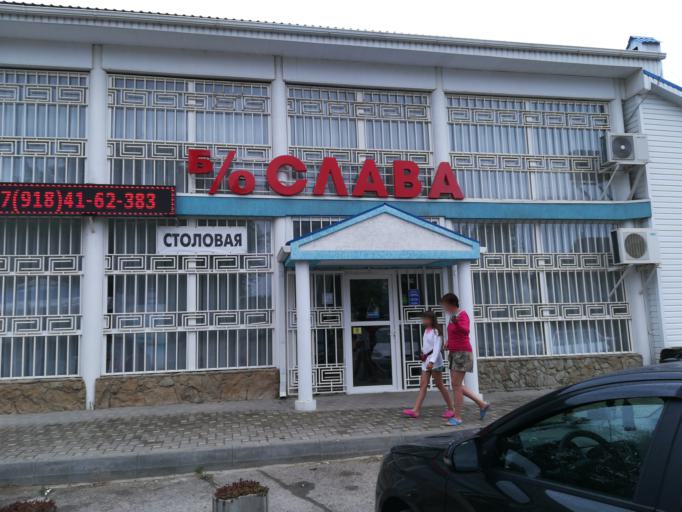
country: RU
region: Krasnodarskiy
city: Vityazevo
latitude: 44.9898
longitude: 37.2469
